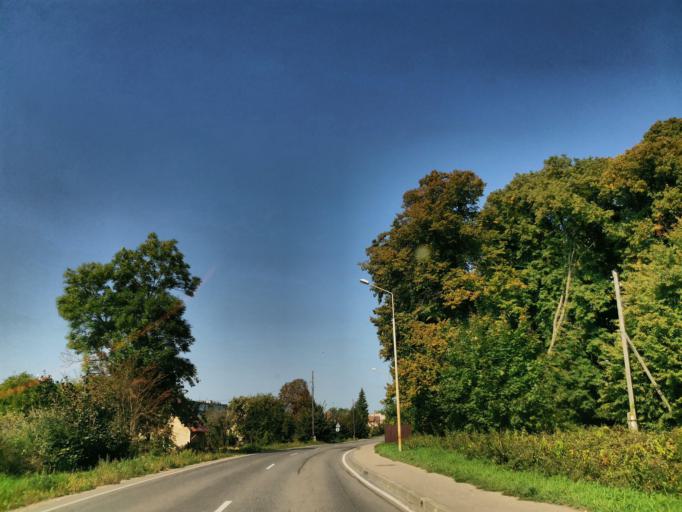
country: RU
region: Kaliningrad
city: Neman
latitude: 55.0298
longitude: 22.0477
